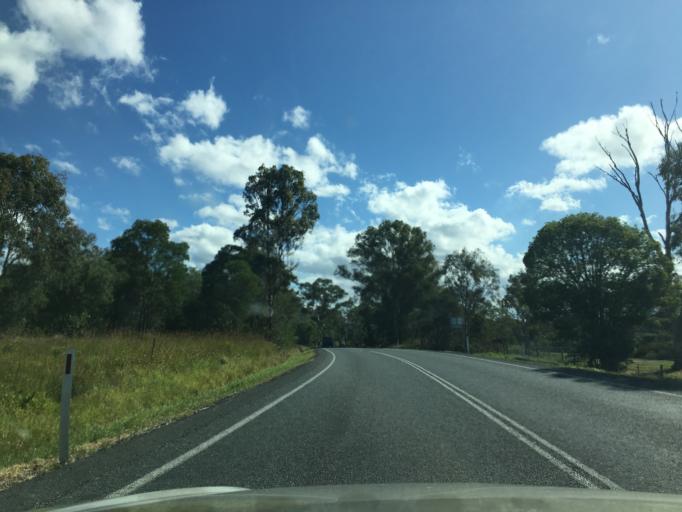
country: AU
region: Queensland
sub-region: Logan
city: Chambers Flat
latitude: -27.7551
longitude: 153.1188
